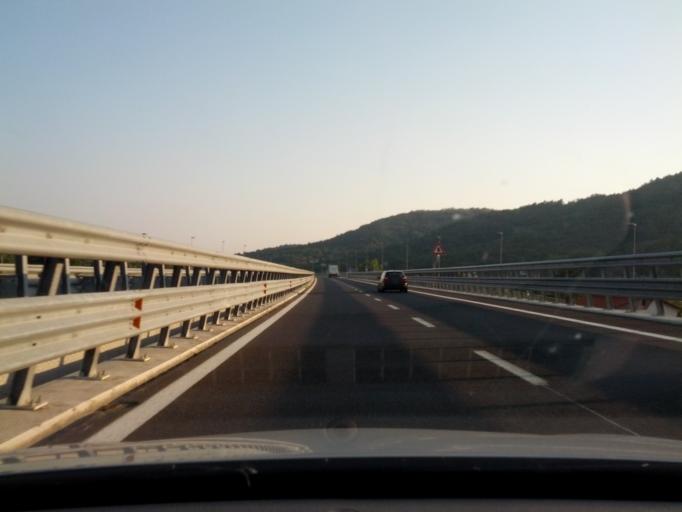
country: SI
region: Koper-Capodistria
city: Spodnje Skofije
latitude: 45.5913
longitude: 13.8002
